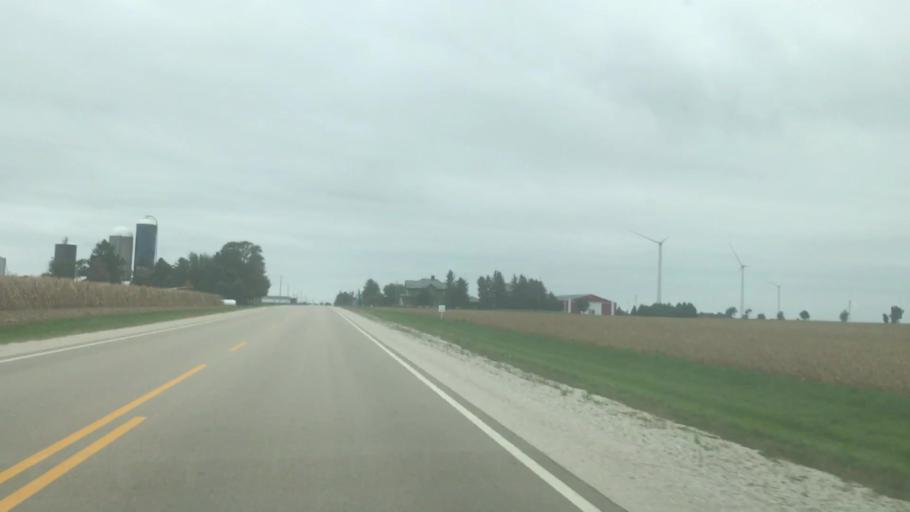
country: US
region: Wisconsin
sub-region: Fond du Lac County
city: Oakfield
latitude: 43.6290
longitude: -88.5417
